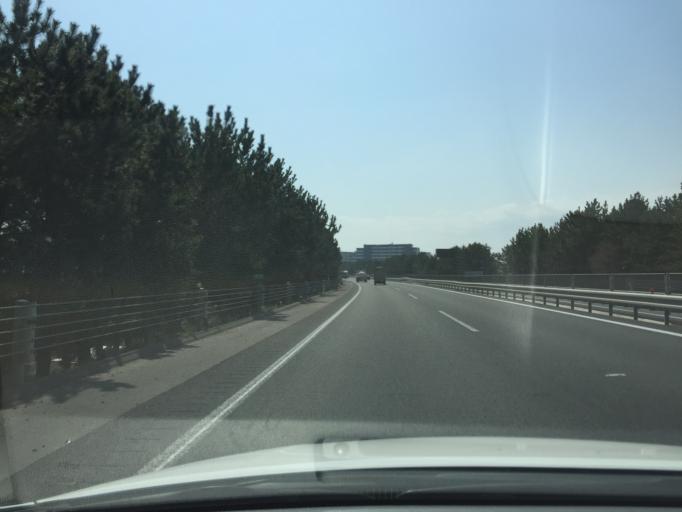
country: JP
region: Miyagi
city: Sendai-shi
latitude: 38.2423
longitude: 140.9522
